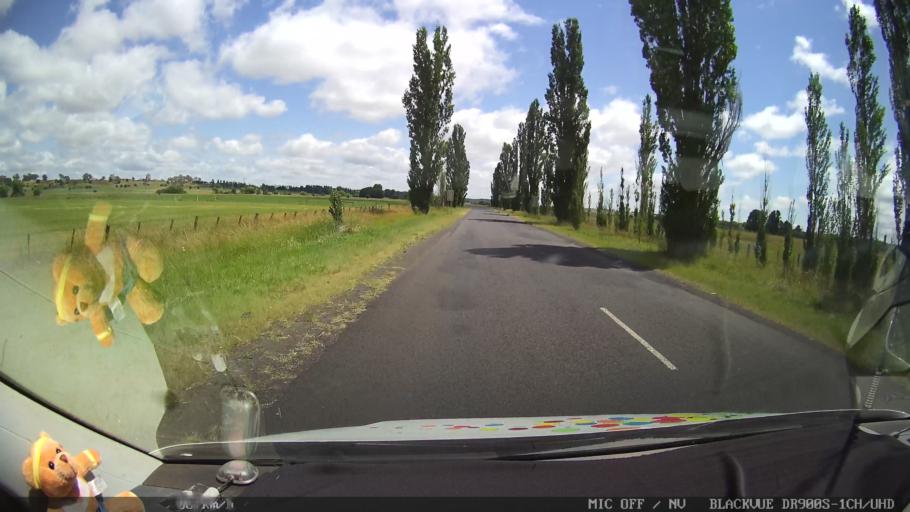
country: AU
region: New South Wales
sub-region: Glen Innes Severn
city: Glen Innes
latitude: -29.7210
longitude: 151.7267
